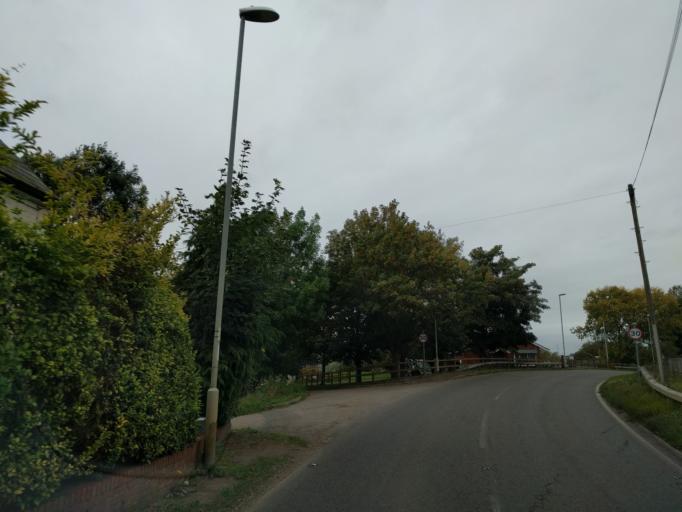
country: GB
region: England
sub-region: Cambridgeshire
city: Earith
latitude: 52.3519
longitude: 0.0453
